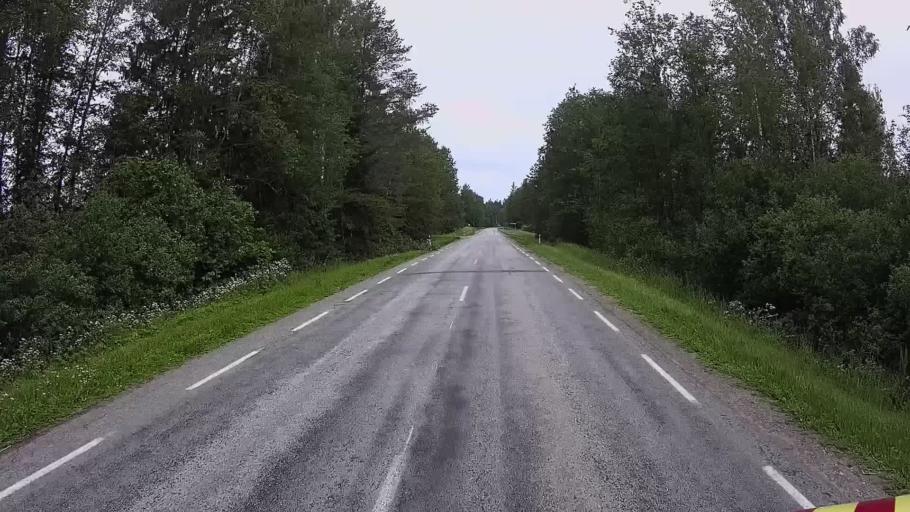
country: EE
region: Viljandimaa
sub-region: Karksi vald
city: Karksi-Nuia
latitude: 58.2132
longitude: 25.6205
